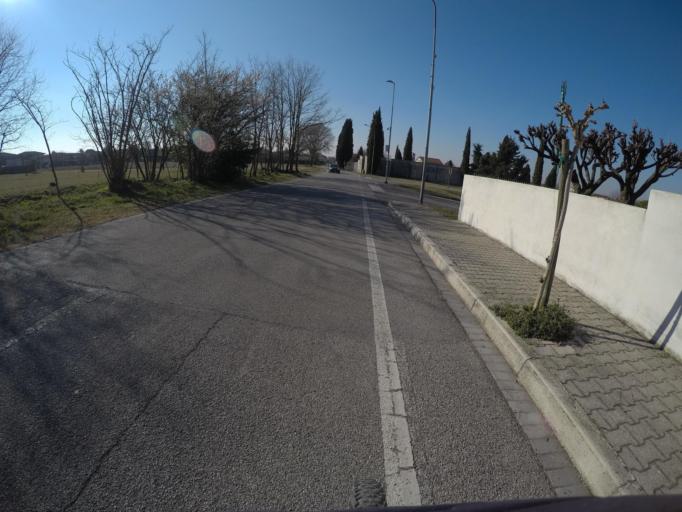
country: IT
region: Friuli Venezia Giulia
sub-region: Provincia di Udine
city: Basaldella
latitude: 46.0206
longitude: 13.2111
